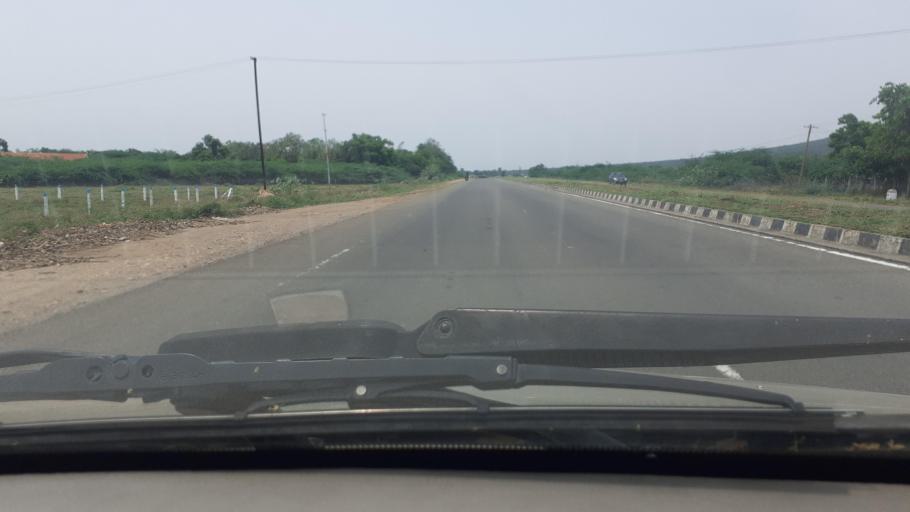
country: IN
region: Tamil Nadu
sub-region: Thoothukkudi
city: Srivaikuntam
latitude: 8.7213
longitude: 77.8596
